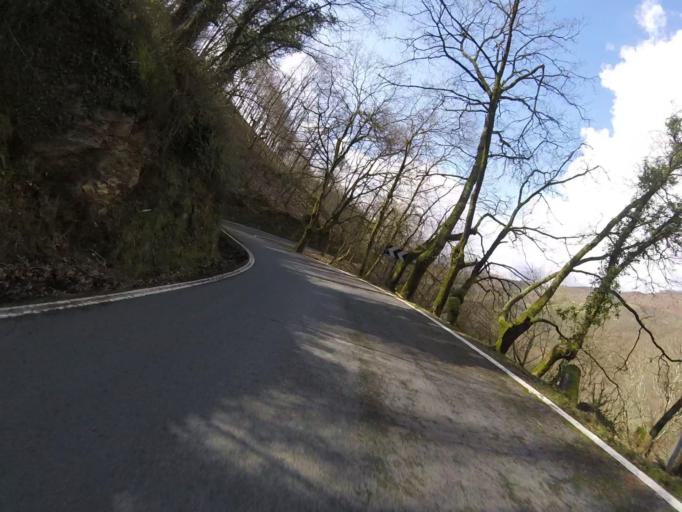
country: ES
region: Navarre
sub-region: Provincia de Navarra
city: Etxalar
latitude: 43.2493
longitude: -1.6135
